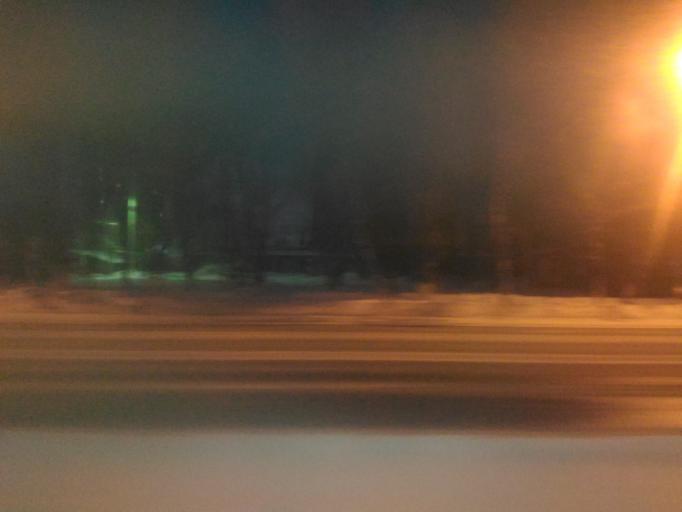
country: RU
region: Ulyanovsk
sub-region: Ulyanovskiy Rayon
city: Ulyanovsk
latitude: 54.3453
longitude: 48.3734
